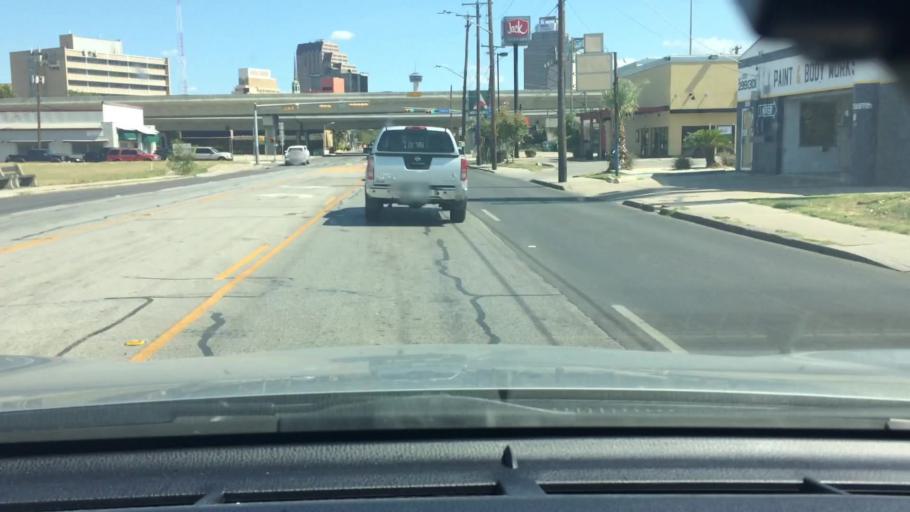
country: US
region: Texas
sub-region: Bexar County
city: San Antonio
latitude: 29.4365
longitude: -98.4966
